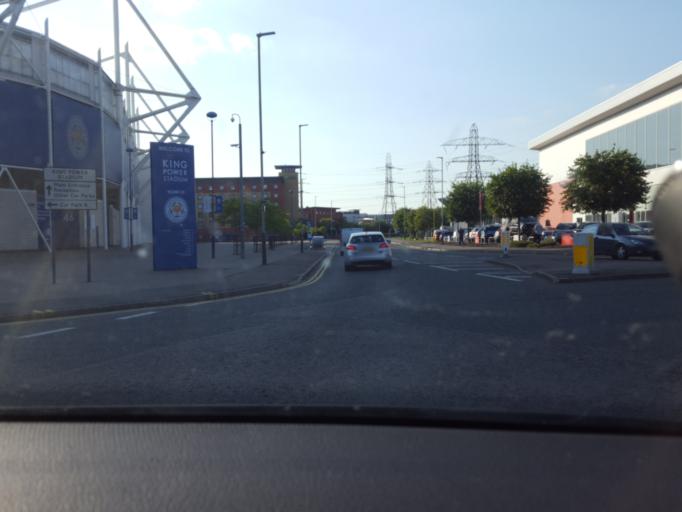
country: GB
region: England
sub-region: City of Leicester
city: Leicester
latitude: 52.6206
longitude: -1.1400
